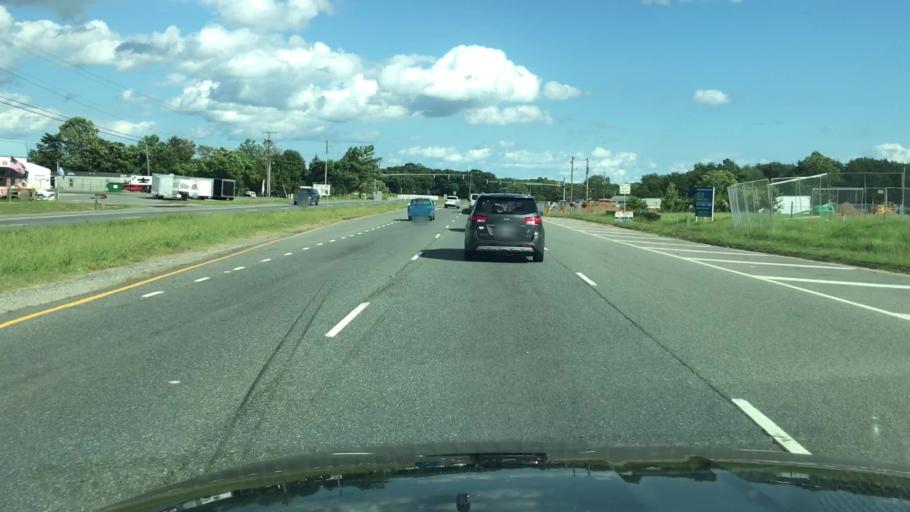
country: US
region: Virginia
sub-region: Stafford County
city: Falmouth
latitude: 38.3703
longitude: -77.5266
